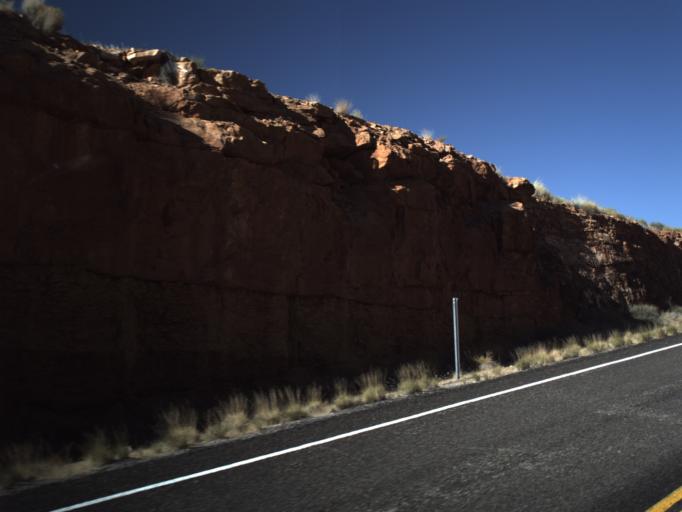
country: US
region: Utah
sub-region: San Juan County
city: Blanding
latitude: 37.8944
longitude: -110.3752
